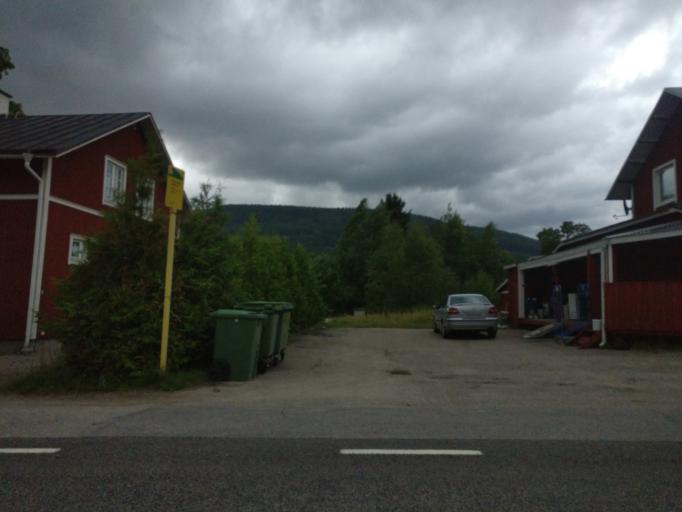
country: SE
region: Vaermland
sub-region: Torsby Kommun
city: Torsby
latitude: 60.7301
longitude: 12.8712
